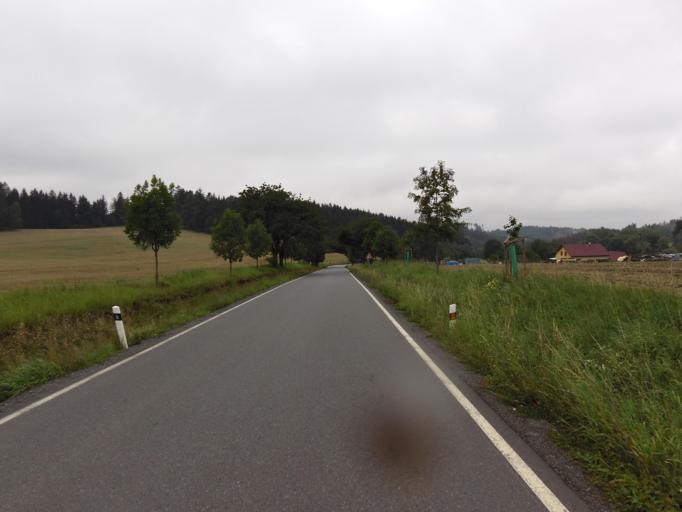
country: CZ
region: Central Bohemia
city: Votice
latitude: 49.6188
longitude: 14.6702
